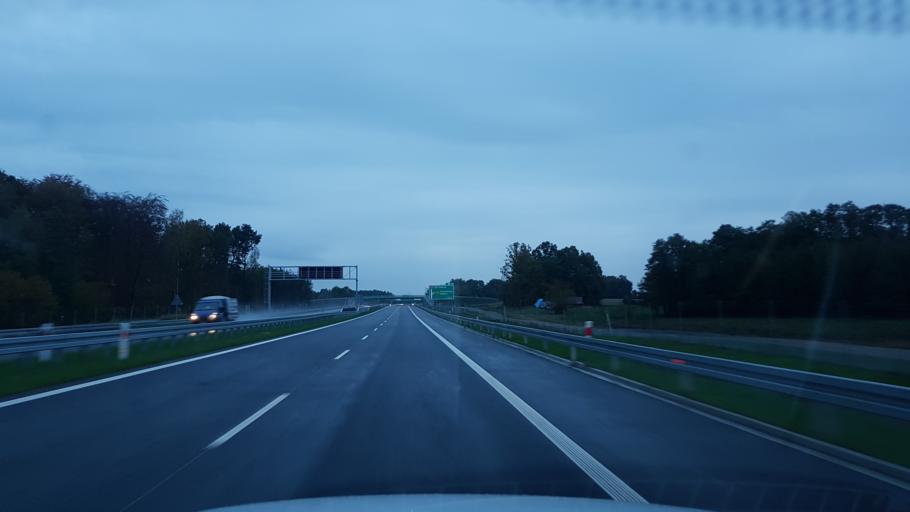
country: PL
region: West Pomeranian Voivodeship
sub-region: Powiat gryficki
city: Brojce
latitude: 53.9331
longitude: 15.3925
